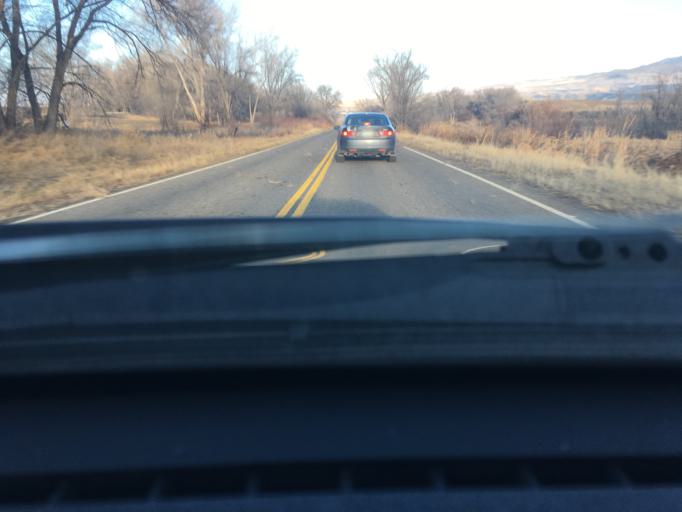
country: US
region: Colorado
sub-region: Delta County
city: Delta
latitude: 38.7431
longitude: -108.1127
